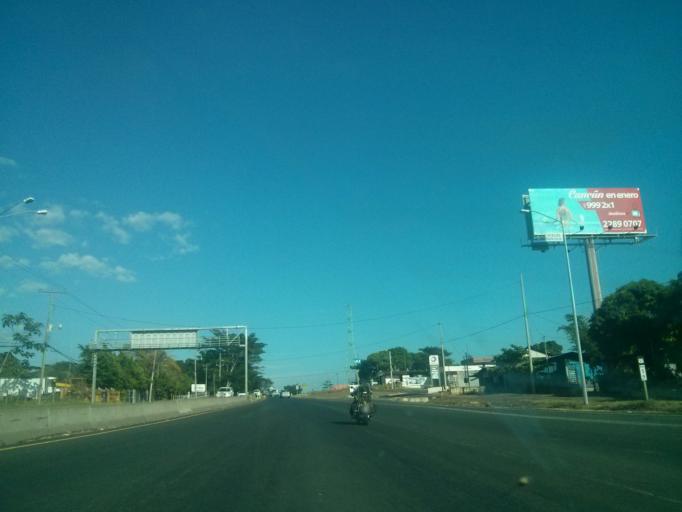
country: CR
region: Alajuela
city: Orotina
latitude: 9.8885
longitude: -84.5693
